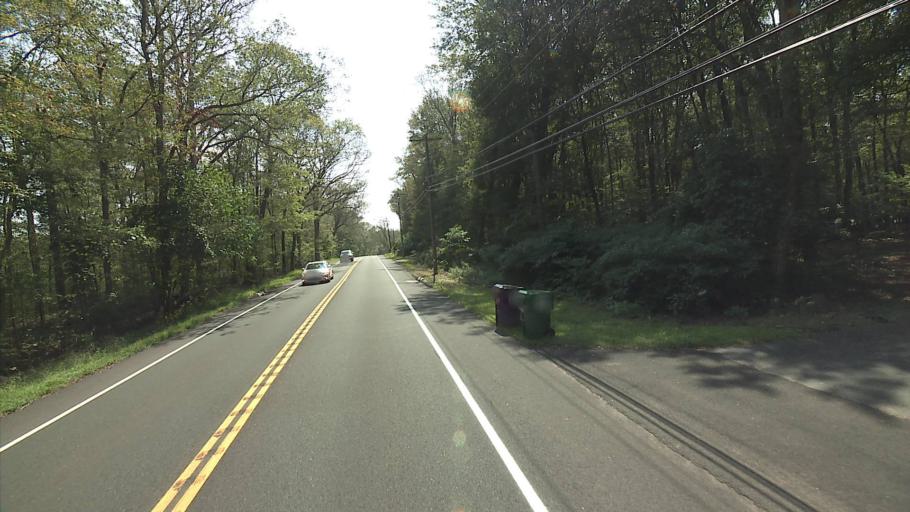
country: US
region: Connecticut
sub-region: New Haven County
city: Guilford
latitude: 41.3848
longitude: -72.6441
